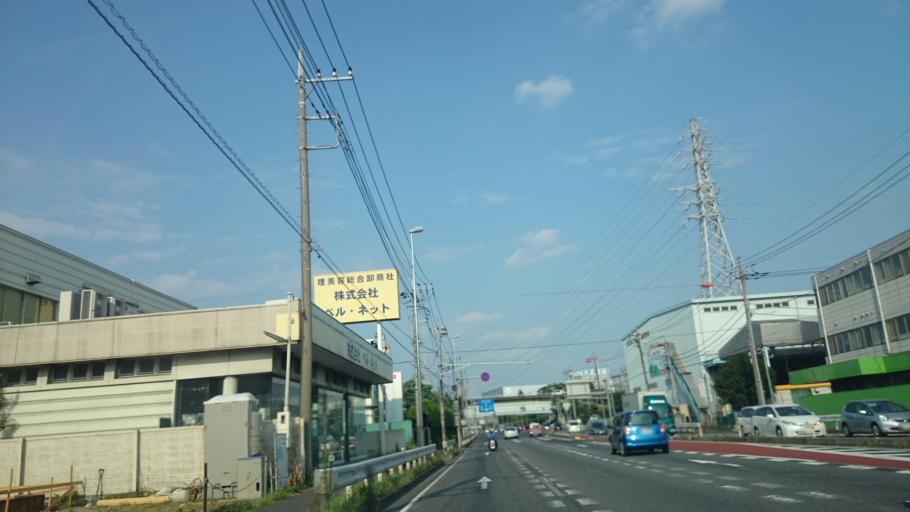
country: JP
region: Saitama
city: Ageoshimo
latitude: 35.9550
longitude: 139.6113
